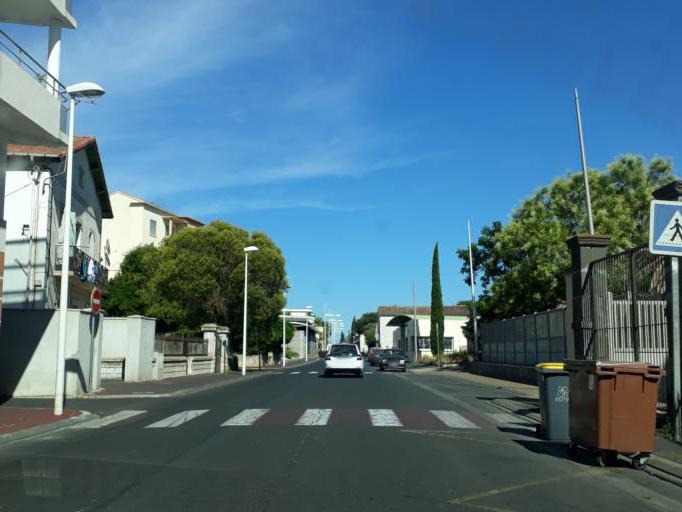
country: FR
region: Languedoc-Roussillon
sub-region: Departement de l'Herault
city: Agde
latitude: 43.3117
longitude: 3.4742
